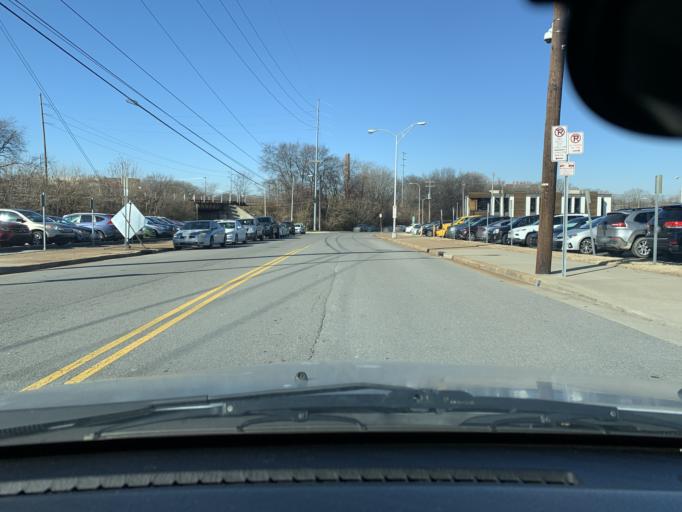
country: US
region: Tennessee
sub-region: Davidson County
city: Nashville
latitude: 36.1638
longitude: -86.7881
